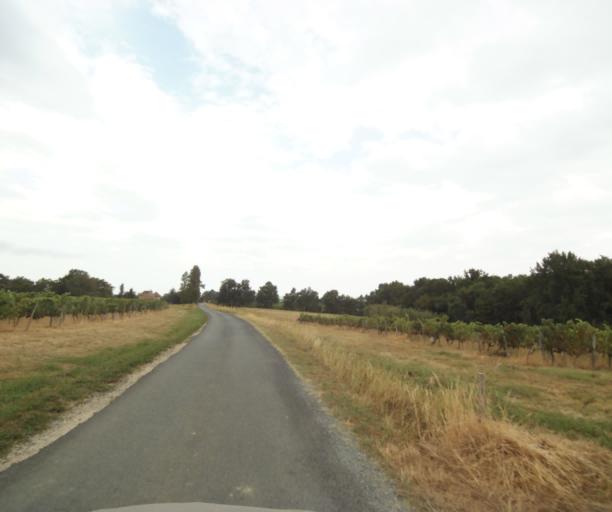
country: FR
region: Aquitaine
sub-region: Departement de la Gironde
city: Creon
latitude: 44.7528
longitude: -0.3447
